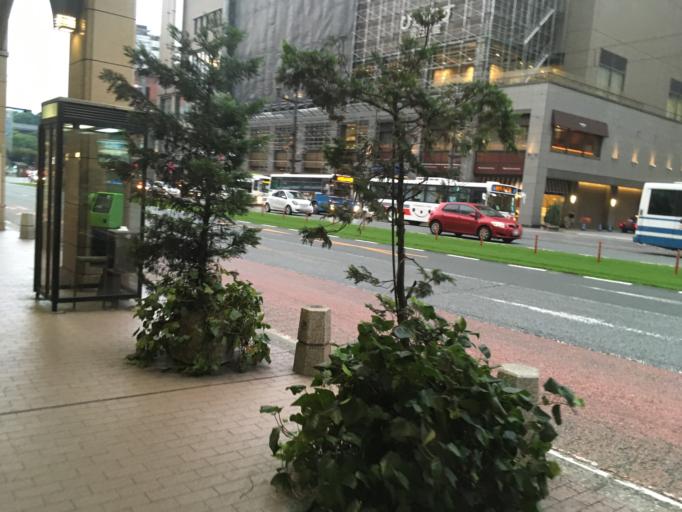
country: JP
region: Kumamoto
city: Kumamoto
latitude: 32.8027
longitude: 130.7115
